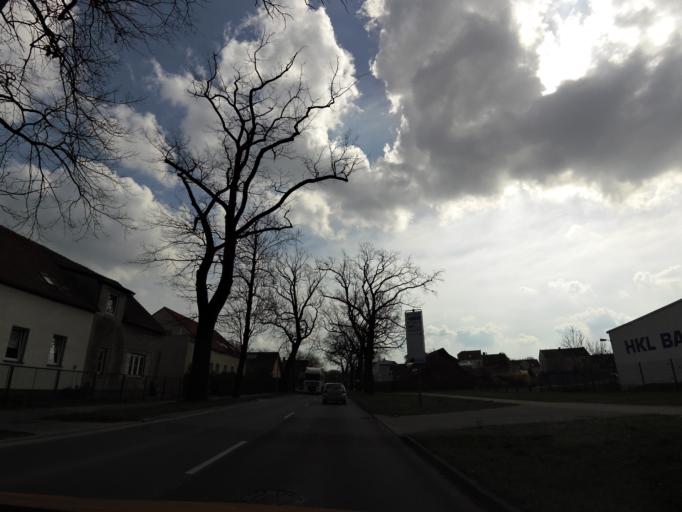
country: DE
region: Brandenburg
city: Petershagen
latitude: 52.4927
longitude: 13.7854
